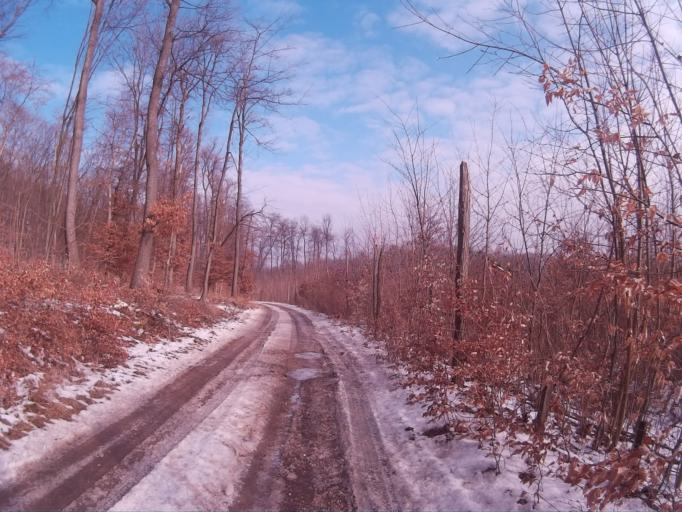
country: HU
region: Komarom-Esztergom
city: Tardos
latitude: 47.6812
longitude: 18.5071
